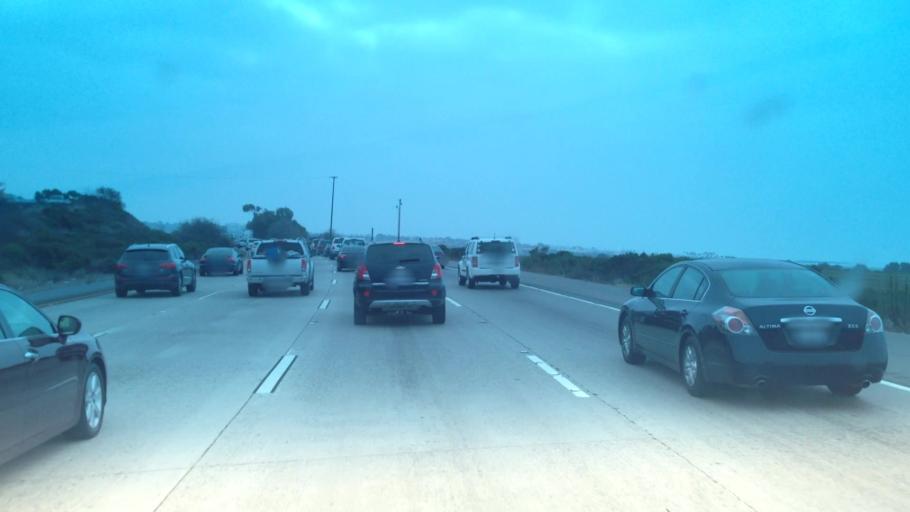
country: US
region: California
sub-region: San Diego County
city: Camp Pendleton South
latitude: 33.2415
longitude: -117.4151
